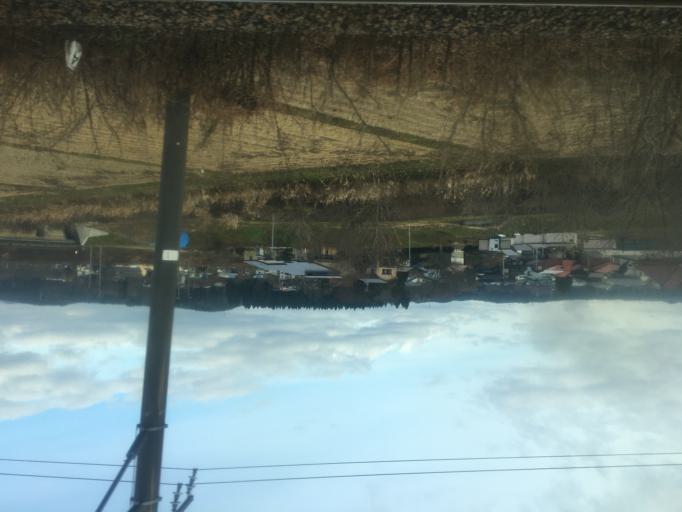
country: JP
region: Akita
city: Takanosu
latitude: 40.2558
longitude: 140.4032
